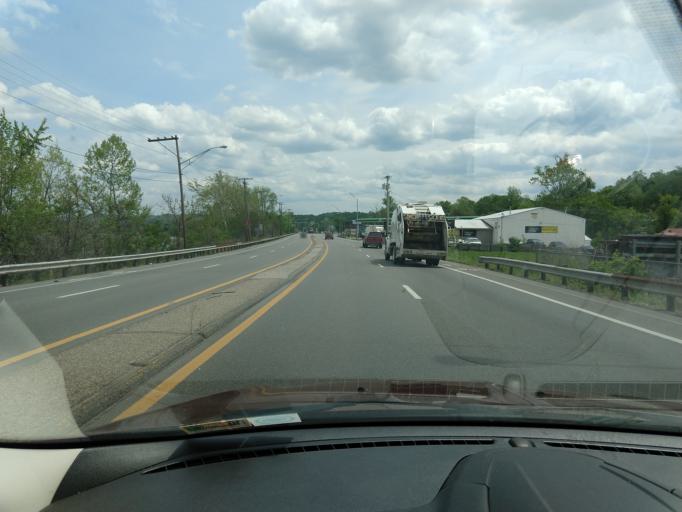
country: US
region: West Virginia
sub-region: Kanawha County
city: Dunbar
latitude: 38.3556
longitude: -81.7514
